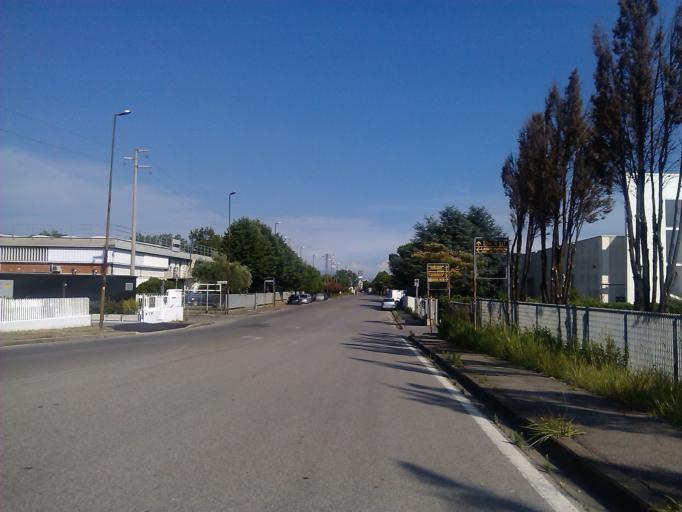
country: IT
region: Tuscany
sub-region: Province of Florence
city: Campi Bisenzio
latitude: 43.8507
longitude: 11.1286
